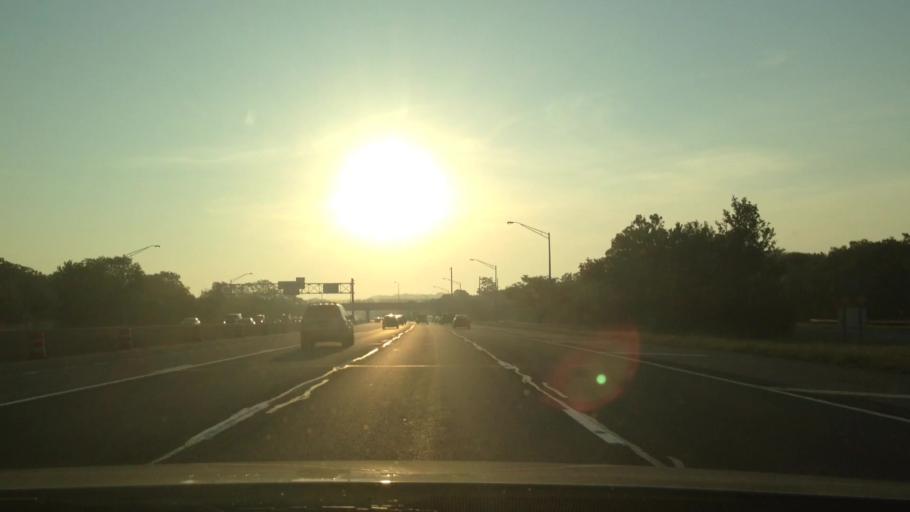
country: US
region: New York
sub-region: Suffolk County
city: Islandia
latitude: 40.8086
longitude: -73.1649
